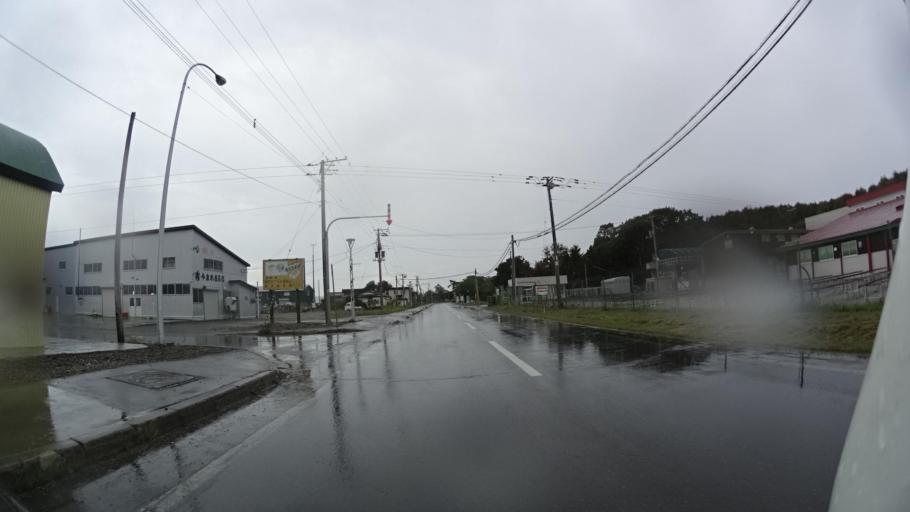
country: JP
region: Hokkaido
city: Kitami
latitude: 44.1884
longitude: 143.7395
